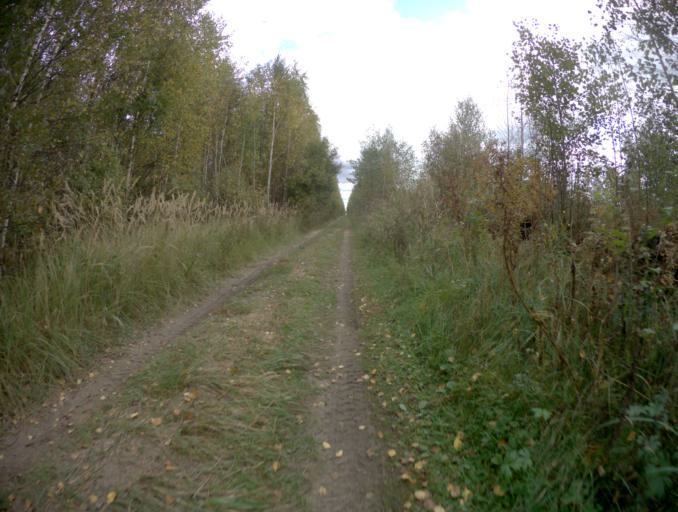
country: RU
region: Vladimir
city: Urshel'skiy
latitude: 55.7477
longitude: 40.0896
